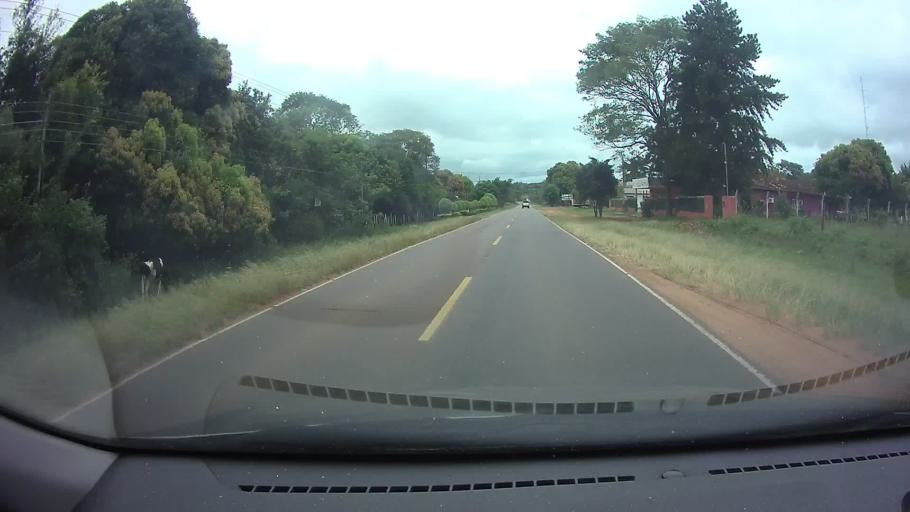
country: PY
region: Central
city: Nueva Italia
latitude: -25.5882
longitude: -57.5074
